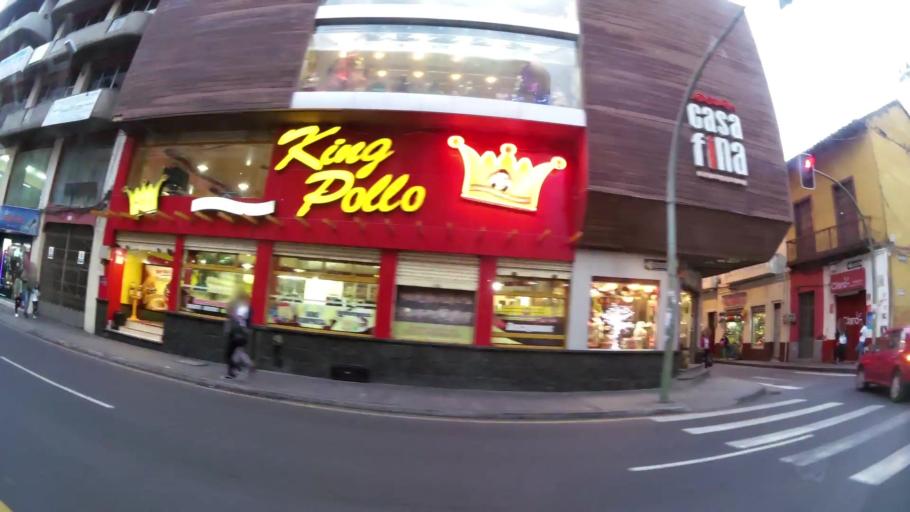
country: EC
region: Tungurahua
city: Ambato
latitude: -1.2426
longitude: -78.6274
